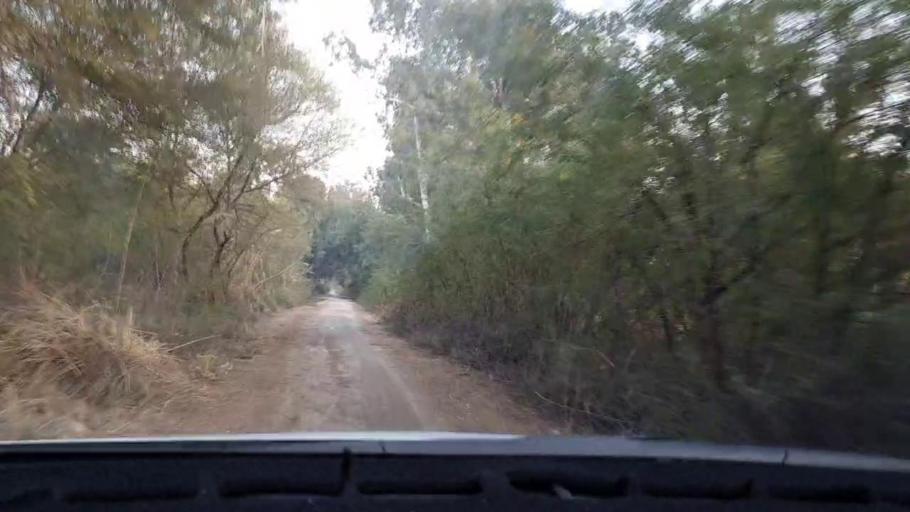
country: PK
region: Sindh
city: Tando Mittha Khan
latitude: 25.8639
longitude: 69.3140
